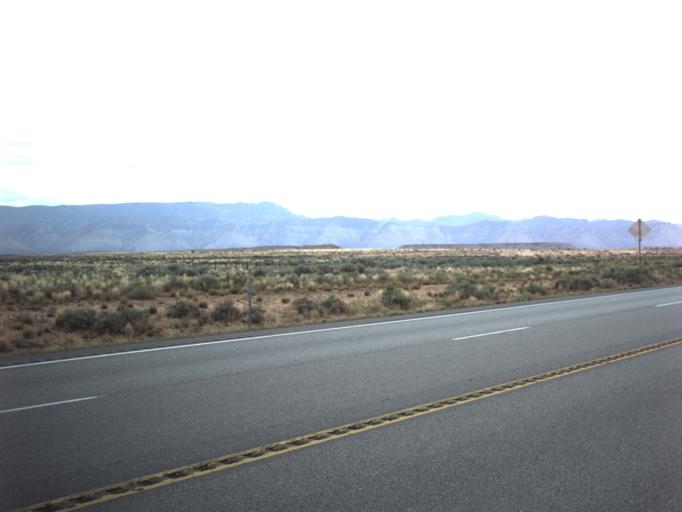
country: US
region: Utah
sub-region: Carbon County
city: East Carbon City
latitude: 39.5084
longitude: -110.5352
